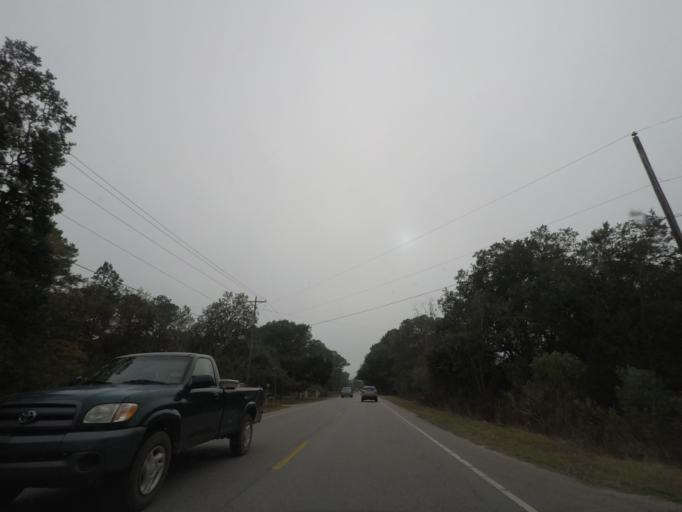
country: US
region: South Carolina
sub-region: Charleston County
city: Seabrook Island
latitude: 32.5276
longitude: -80.2968
